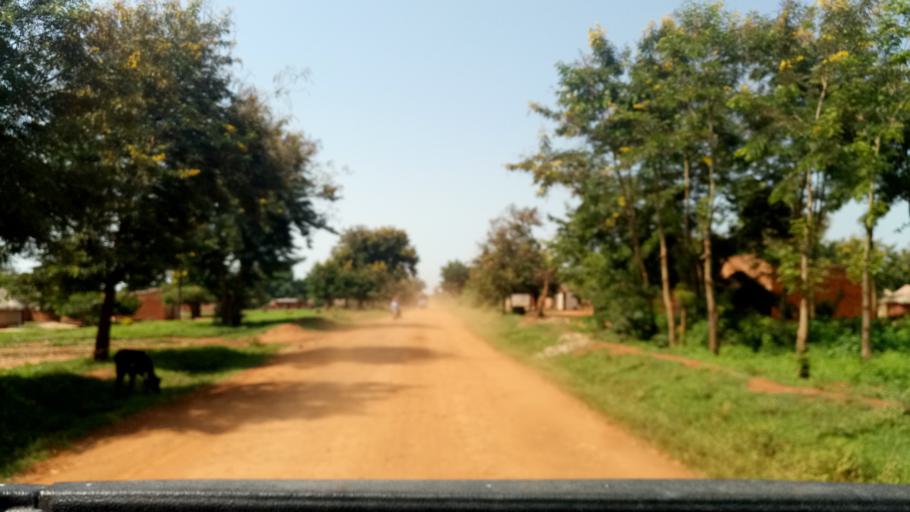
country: UG
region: Eastern Region
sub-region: Kaliro District
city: Kaliro
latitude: 0.9615
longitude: 33.4703
